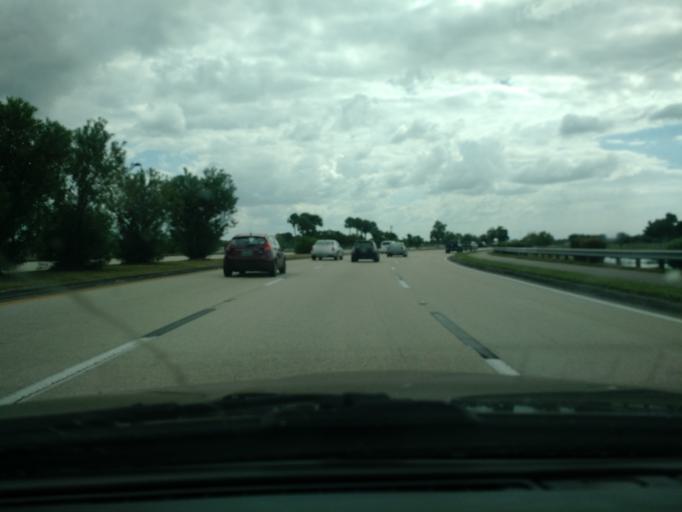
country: US
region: Florida
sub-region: Lee County
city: Pine Manor
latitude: 26.5866
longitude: -81.8686
